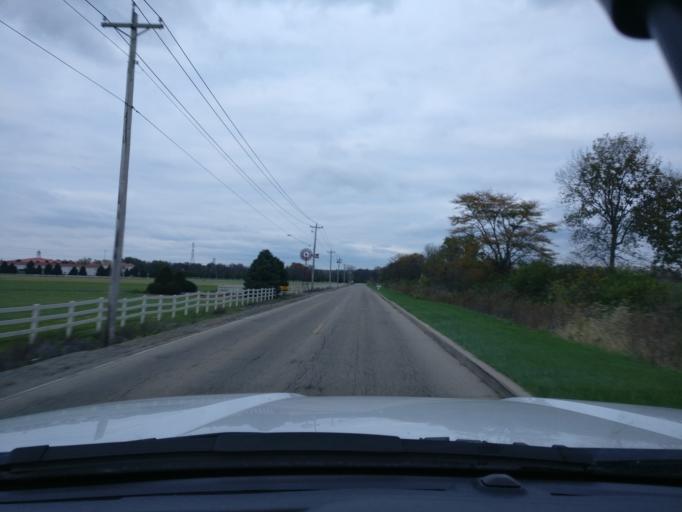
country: US
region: Ohio
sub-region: Butler County
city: Monroe
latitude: 39.4484
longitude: -84.3234
